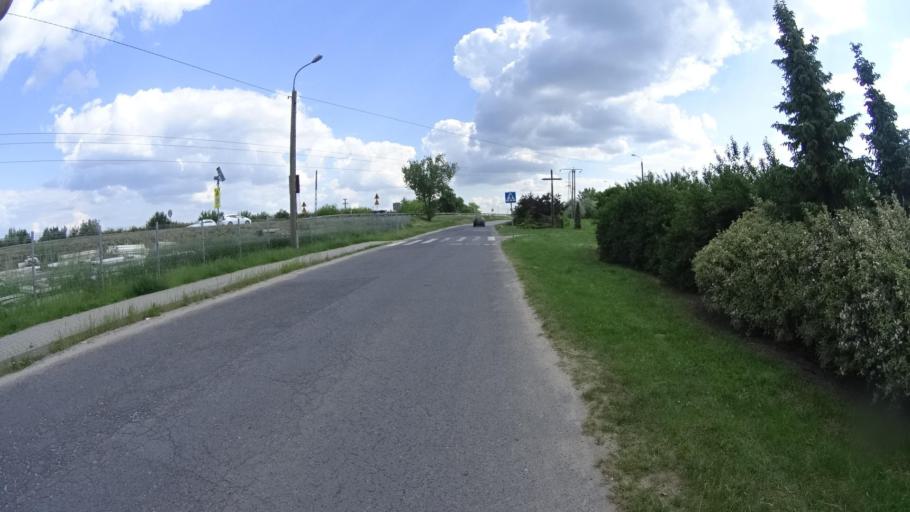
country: PL
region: Masovian Voivodeship
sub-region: Powiat piaseczynski
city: Tarczyn
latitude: 51.9731
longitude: 20.8340
